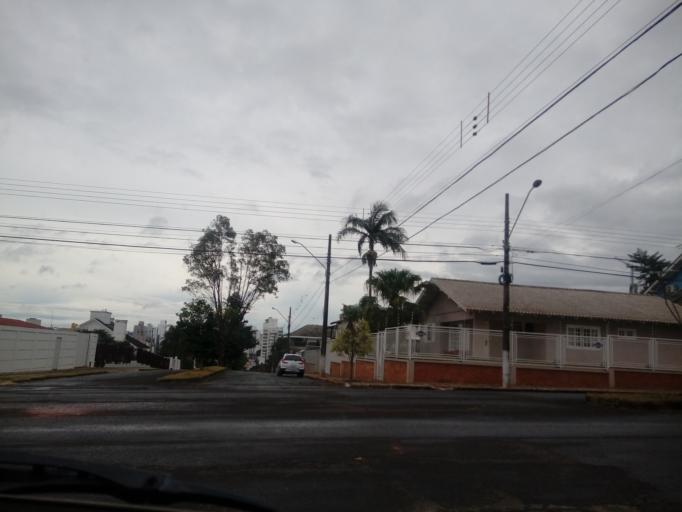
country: BR
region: Santa Catarina
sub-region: Chapeco
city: Chapeco
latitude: -27.1059
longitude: -52.6235
